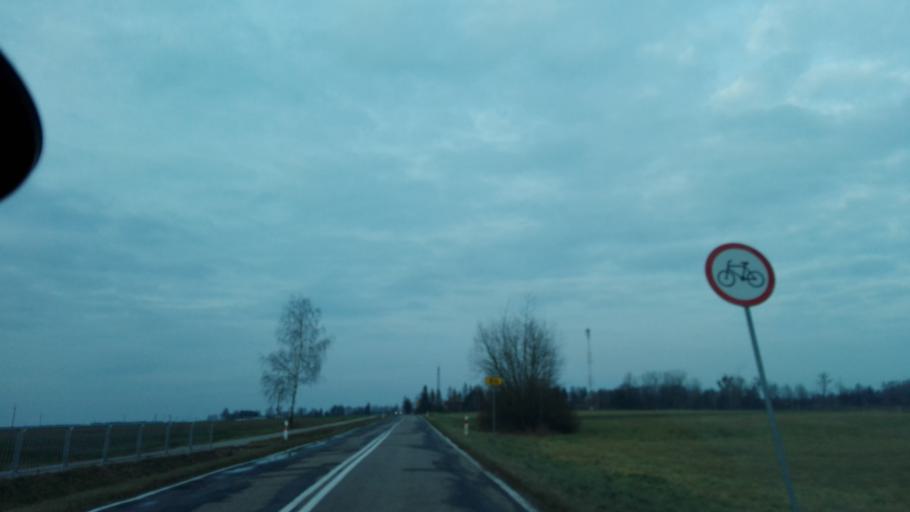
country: PL
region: Lublin Voivodeship
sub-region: Powiat bialski
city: Slawatycze
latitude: 51.6783
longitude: 23.5079
